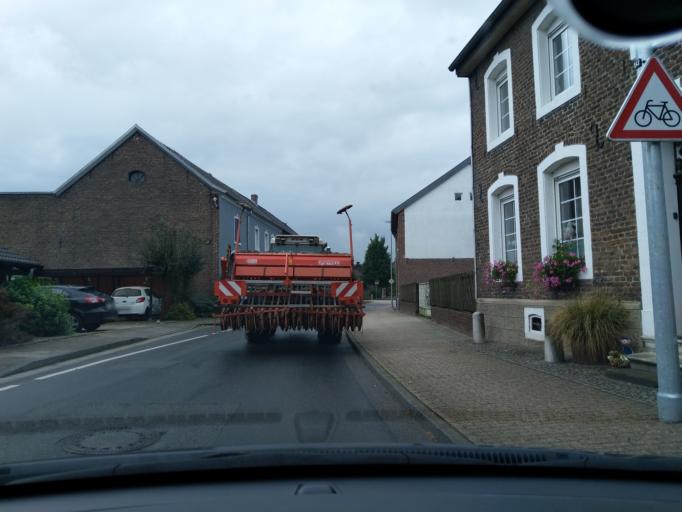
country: DE
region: North Rhine-Westphalia
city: Wegberg
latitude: 51.1052
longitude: 6.2836
